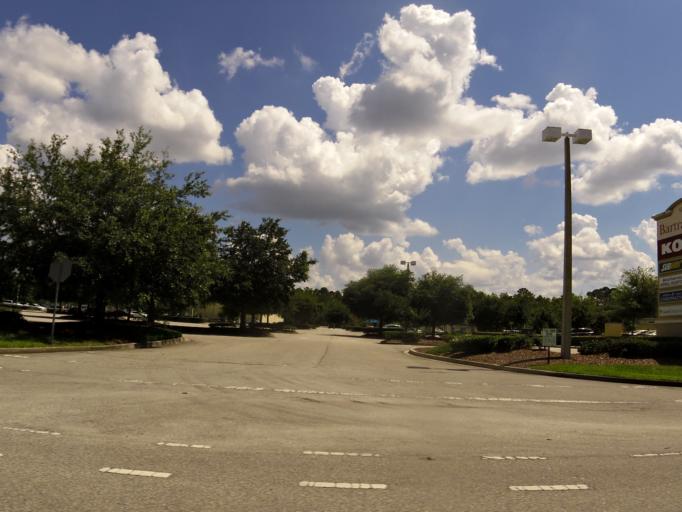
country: US
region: Florida
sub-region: Saint Johns County
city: Fruit Cove
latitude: 30.1429
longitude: -81.5524
